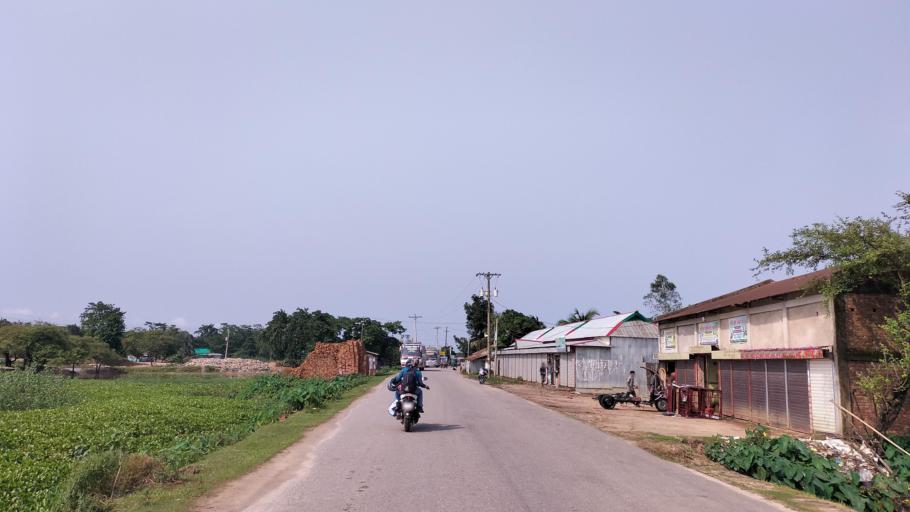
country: BD
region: Dhaka
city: Netrakona
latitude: 25.0699
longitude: 90.8849
